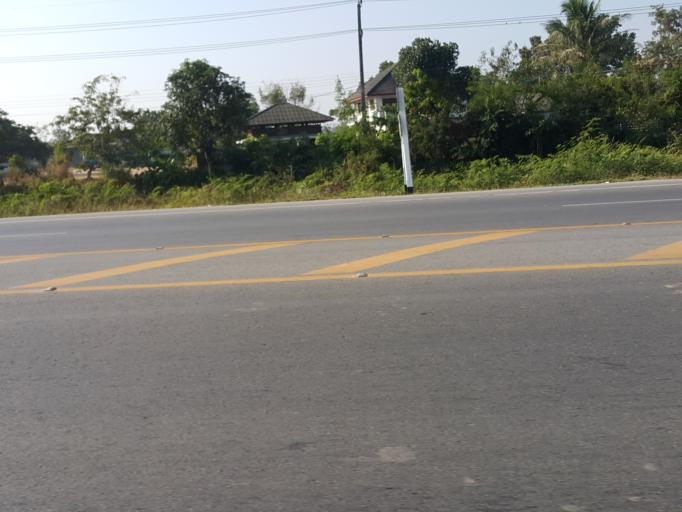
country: TH
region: Chiang Mai
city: San Kamphaeng
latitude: 18.7278
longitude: 99.1005
